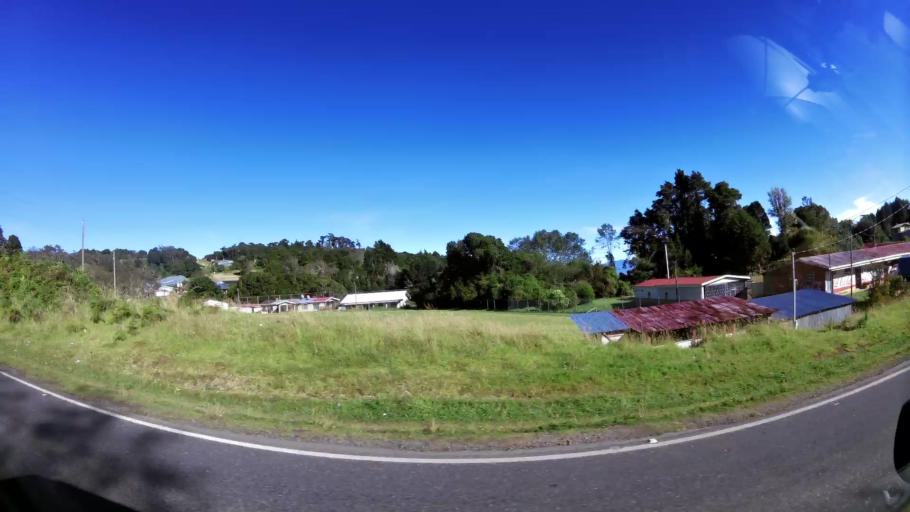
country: CR
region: San Jose
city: San Marcos
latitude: 9.6832
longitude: -83.9175
